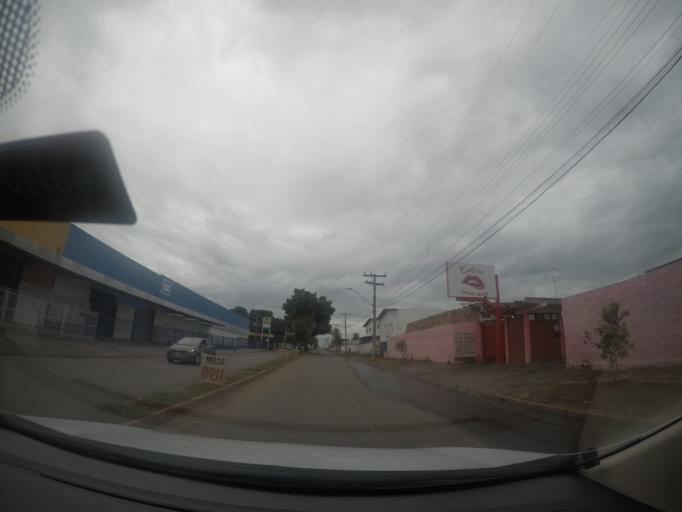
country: BR
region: Goias
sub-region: Goiania
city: Goiania
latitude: -16.6683
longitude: -49.3246
